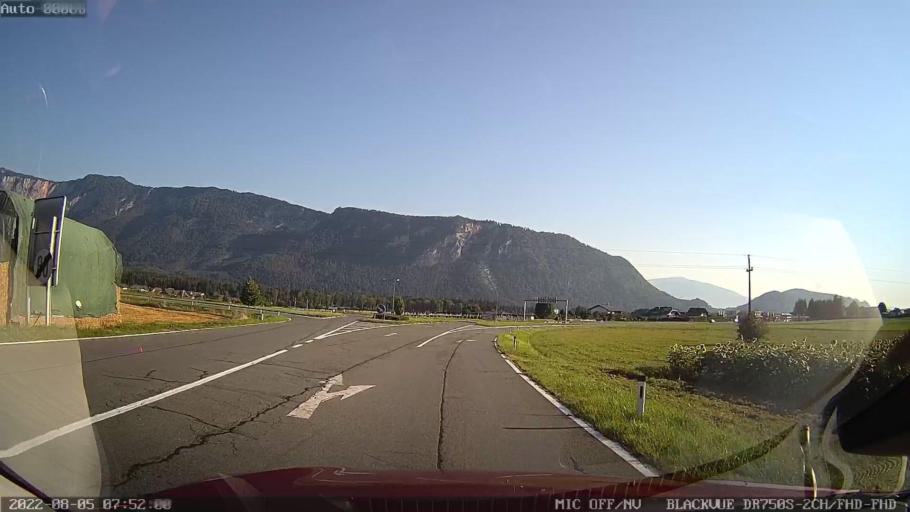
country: AT
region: Carinthia
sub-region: Politischer Bezirk Villach Land
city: Finkenstein am Faaker See
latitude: 46.5552
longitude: 13.7886
